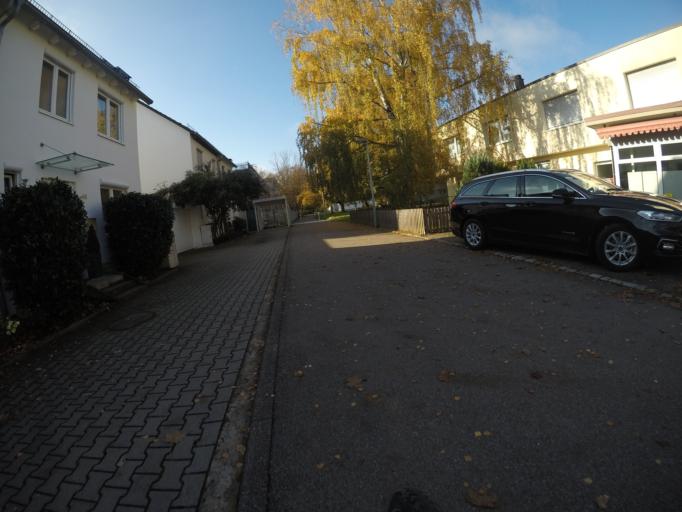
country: DE
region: Baden-Wuerttemberg
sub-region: Regierungsbezirk Stuttgart
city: Steinenbronn
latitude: 48.7167
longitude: 9.1221
